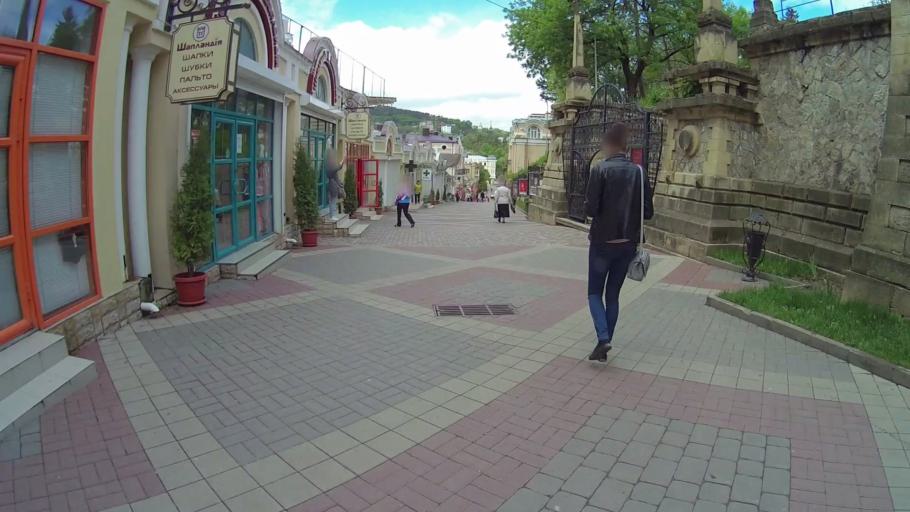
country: RU
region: Stavropol'skiy
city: Kislovodsk
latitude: 43.9009
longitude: 42.7195
